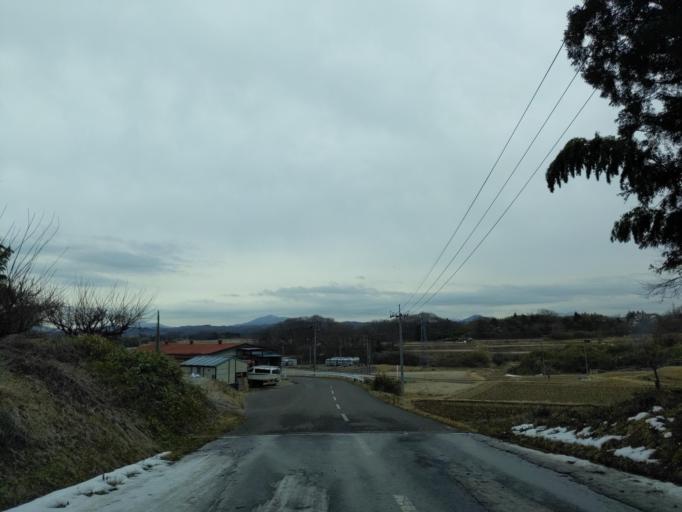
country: JP
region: Fukushima
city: Motomiya
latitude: 37.4640
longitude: 140.3935
